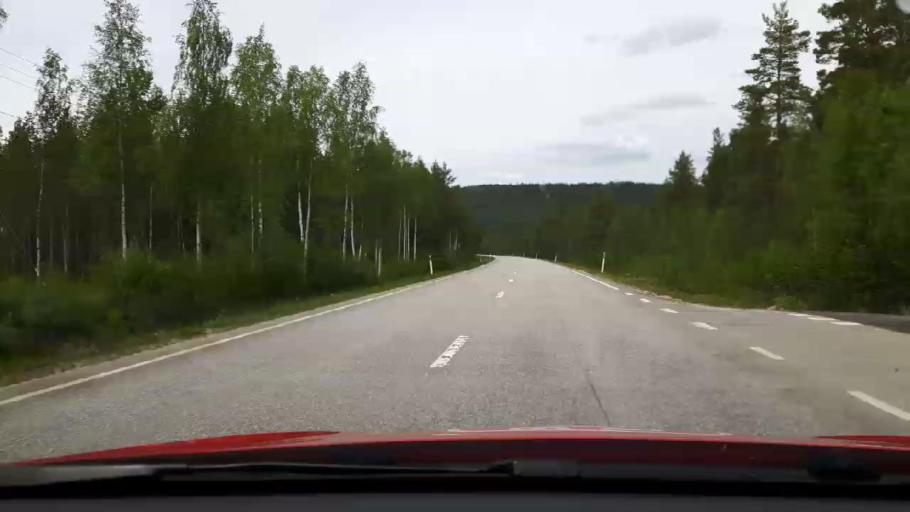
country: SE
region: Jaemtland
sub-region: Harjedalens Kommun
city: Sveg
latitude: 62.0919
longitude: 14.2433
